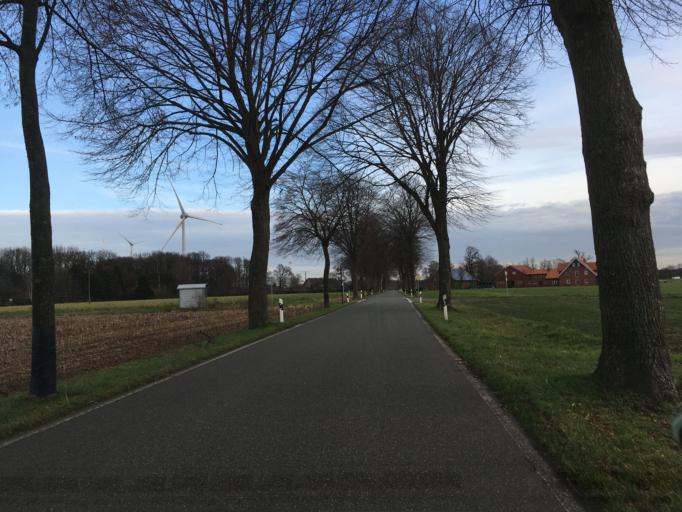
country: DE
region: North Rhine-Westphalia
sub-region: Regierungsbezirk Munster
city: Gescher
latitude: 51.9875
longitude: 7.0359
